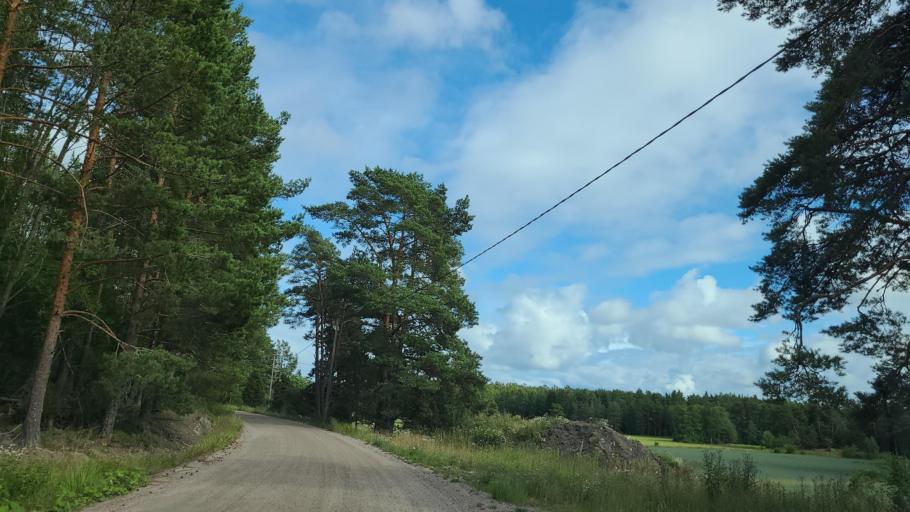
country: FI
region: Varsinais-Suomi
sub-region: Aboland-Turunmaa
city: Nagu
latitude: 60.1419
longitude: 21.7894
